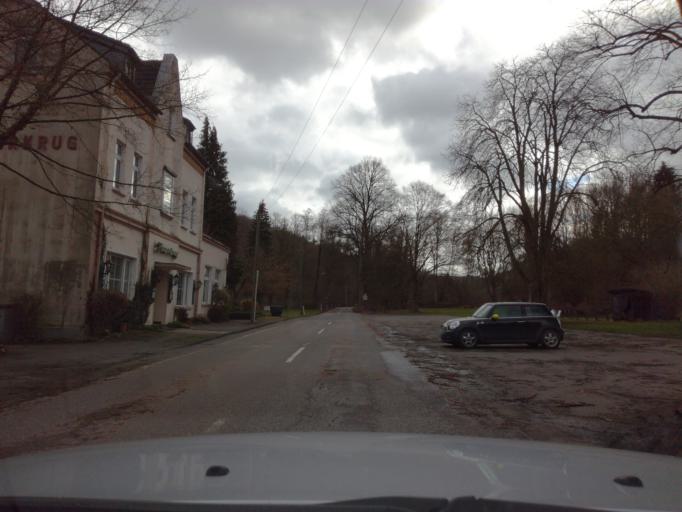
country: DE
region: North Rhine-Westphalia
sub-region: Regierungsbezirk Dusseldorf
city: Velbert
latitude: 51.3773
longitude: 7.0389
